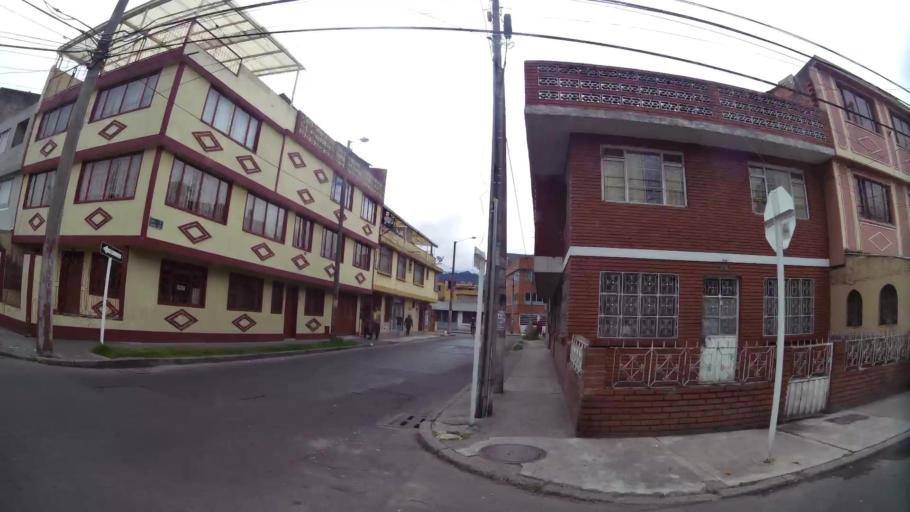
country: CO
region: Bogota D.C.
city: Bogota
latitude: 4.6182
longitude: -74.1117
